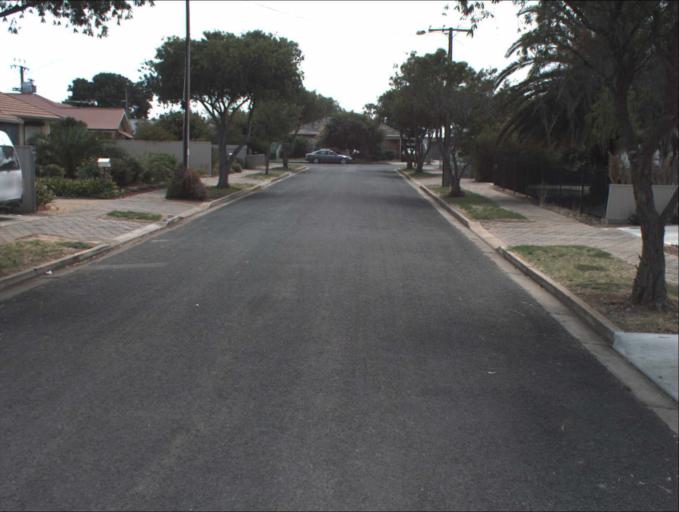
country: AU
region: South Australia
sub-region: Salisbury
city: Ingle Farm
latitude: -34.8518
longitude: 138.6248
